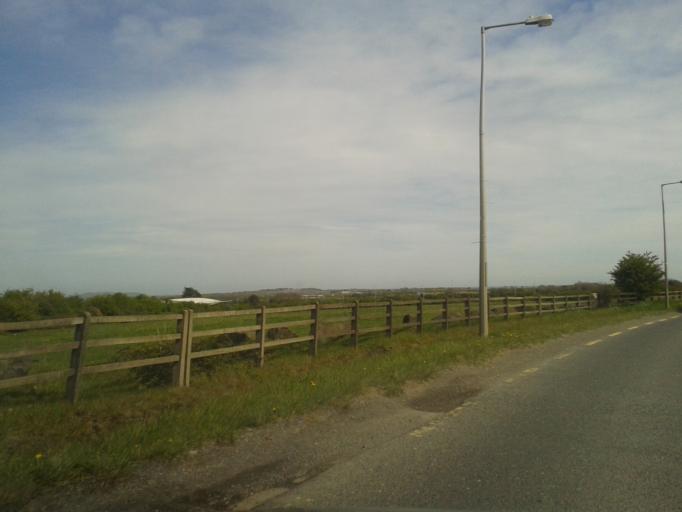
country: IE
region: Leinster
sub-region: Fingal County
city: Swords
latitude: 53.4356
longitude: -6.2317
